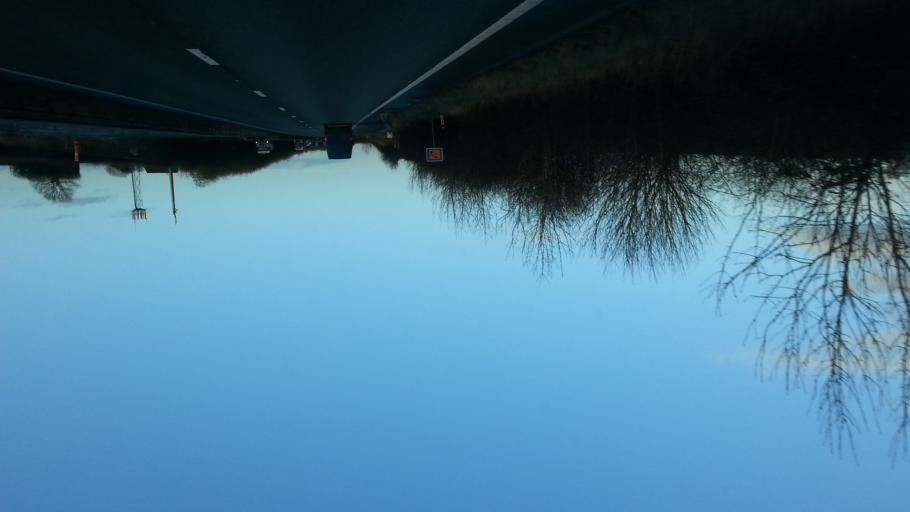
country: GB
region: England
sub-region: Northamptonshire
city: Desborough
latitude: 52.4049
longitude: -0.8689
